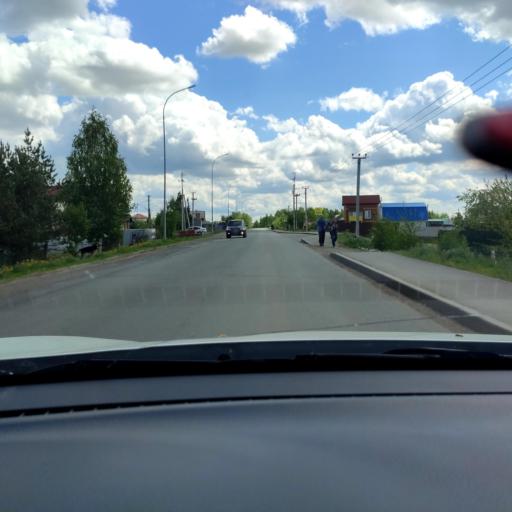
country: RU
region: Tatarstan
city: Stolbishchi
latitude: 55.6964
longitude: 49.1936
